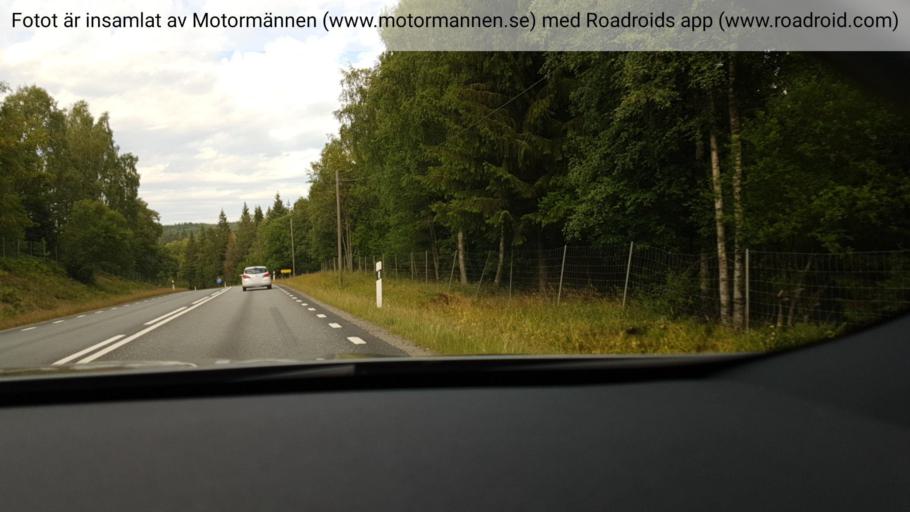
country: SE
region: Joenkoeping
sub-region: Nassjo Kommun
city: Nassjo
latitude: 57.6353
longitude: 14.8219
